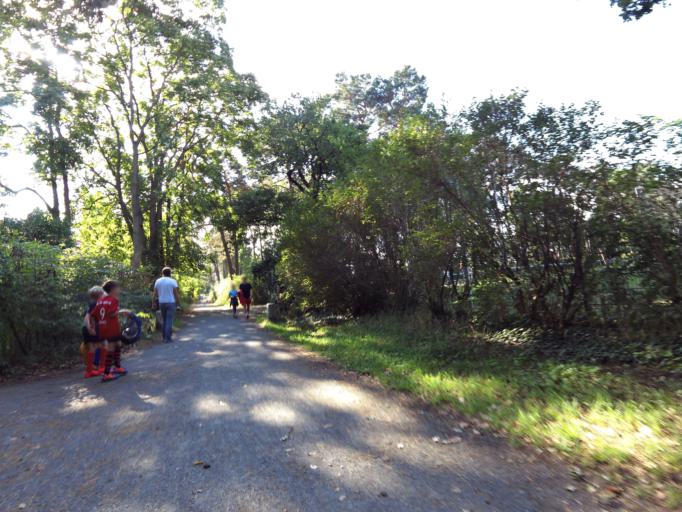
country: DE
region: Berlin
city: Zehlendorf Bezirk
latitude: 52.4444
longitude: 13.2530
